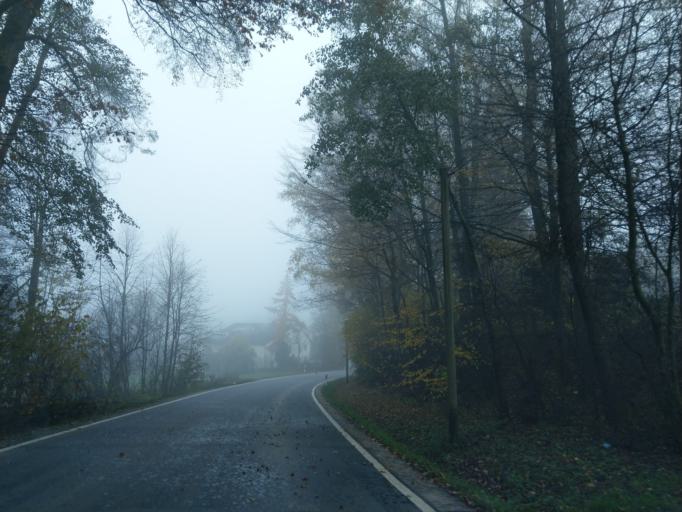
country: DE
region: Bavaria
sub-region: Lower Bavaria
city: Auerbach
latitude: 48.7717
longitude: 13.0919
